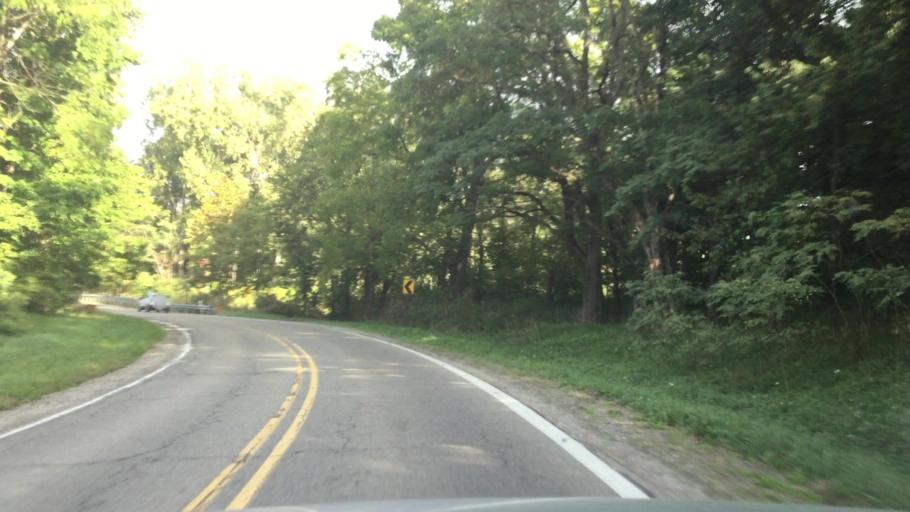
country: US
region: Michigan
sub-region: Livingston County
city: Brighton
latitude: 42.4898
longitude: -83.8531
